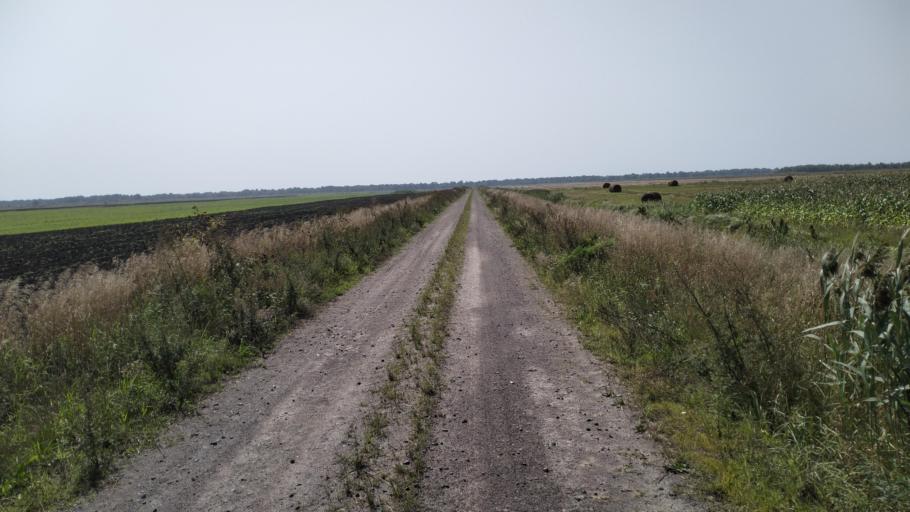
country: BY
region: Brest
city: Davyd-Haradok
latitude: 51.9848
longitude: 27.1638
